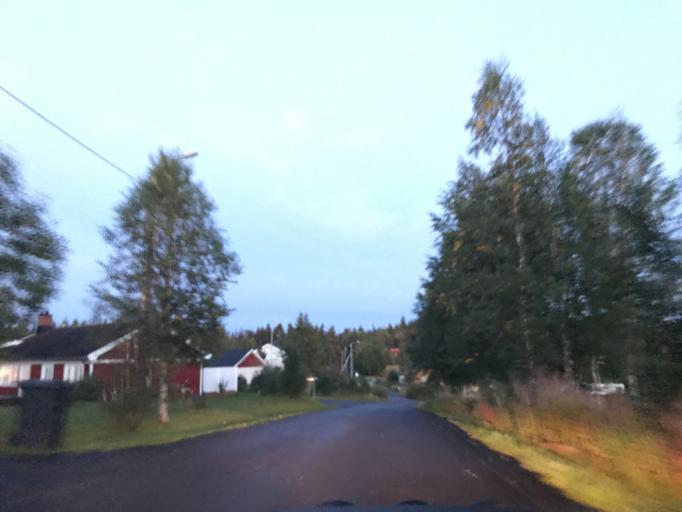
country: SE
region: Norrbotten
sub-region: Gallivare Kommun
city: Malmberget
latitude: 67.6472
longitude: 21.0625
